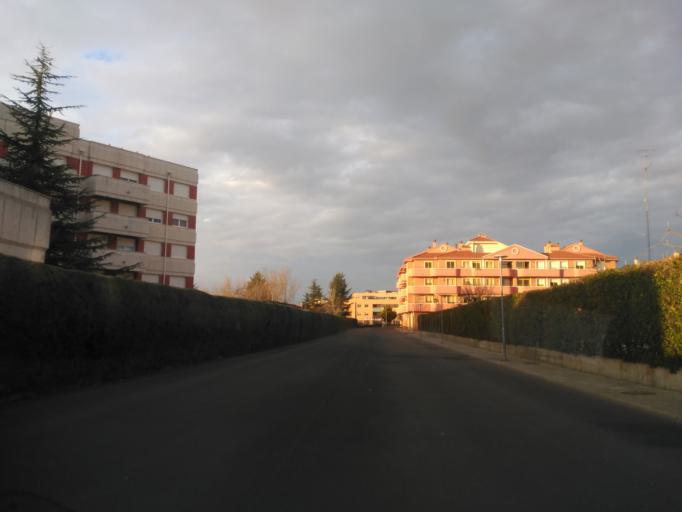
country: ES
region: Castille and Leon
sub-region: Provincia de Salamanca
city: Santa Marta de Tormes
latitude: 40.9490
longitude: -5.6390
